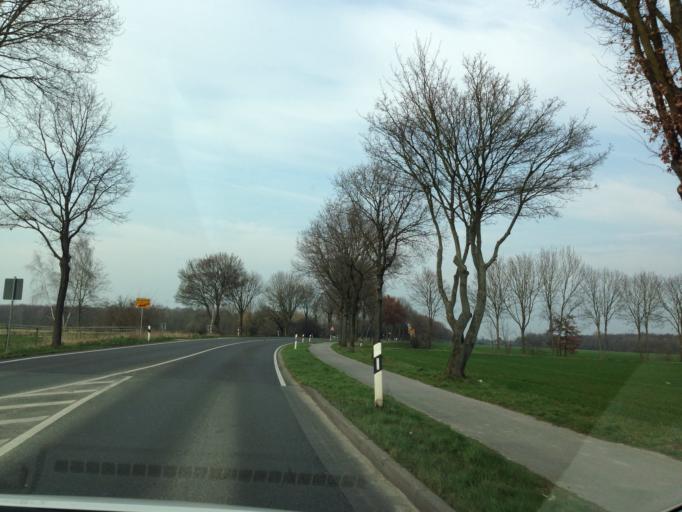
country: DE
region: North Rhine-Westphalia
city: Erkelenz
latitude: 51.0427
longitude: 6.2823
